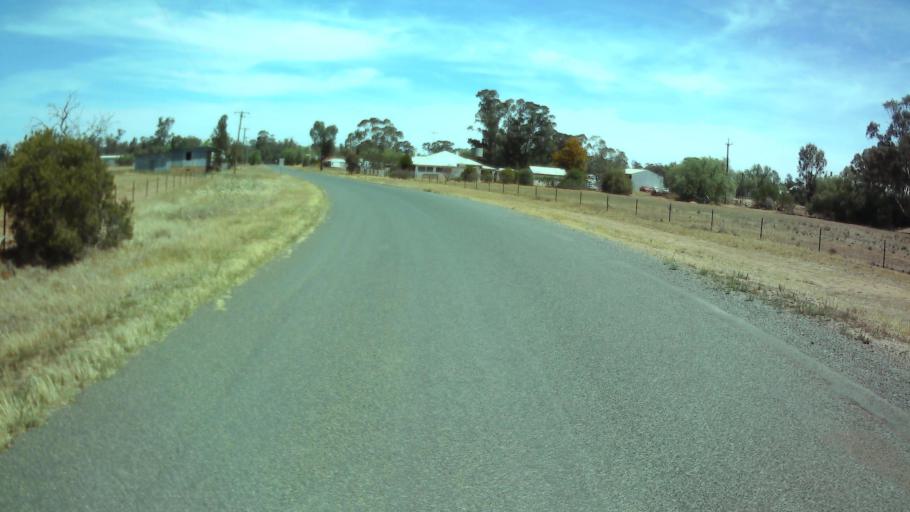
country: AU
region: New South Wales
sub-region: Weddin
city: Grenfell
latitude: -33.8391
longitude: 147.7448
